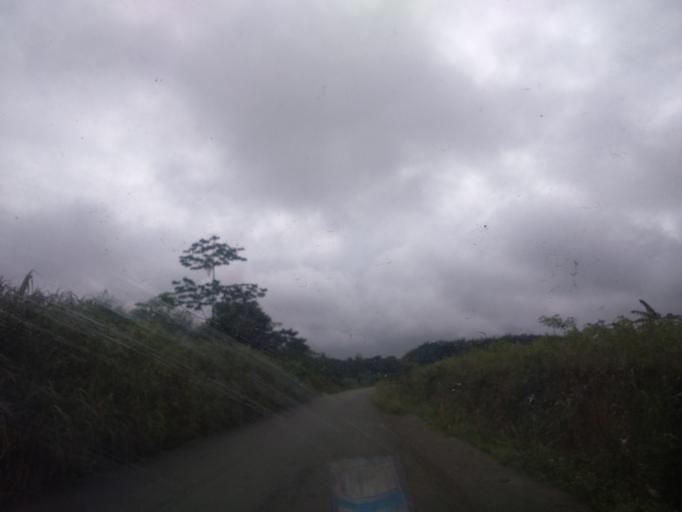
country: CI
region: Sud-Comoe
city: Bonoua
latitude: 5.2842
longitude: -3.4722
